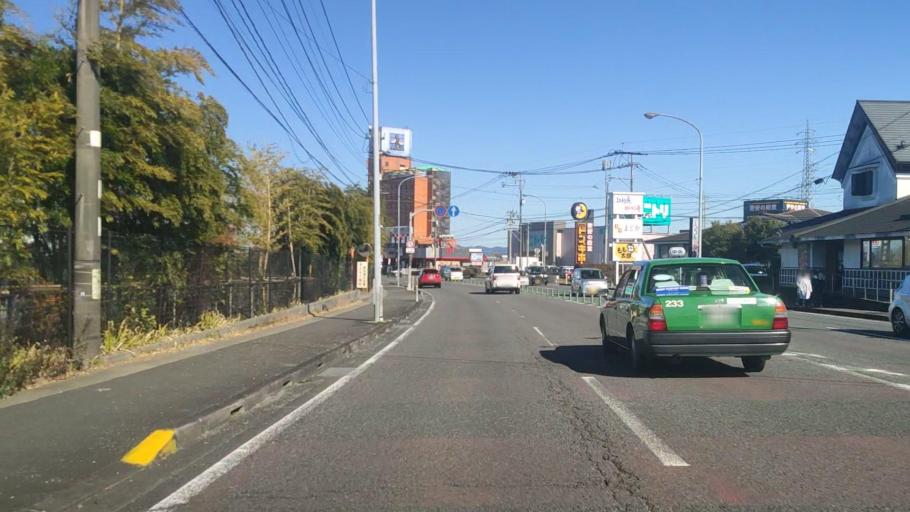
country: JP
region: Miyazaki
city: Miyakonojo
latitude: 31.7462
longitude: 131.0771
